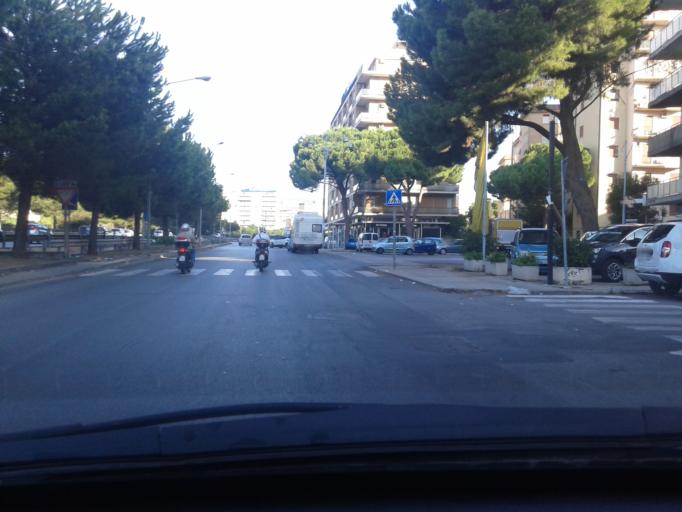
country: IT
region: Sicily
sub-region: Palermo
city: Palermo
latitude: 38.0998
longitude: 13.3324
